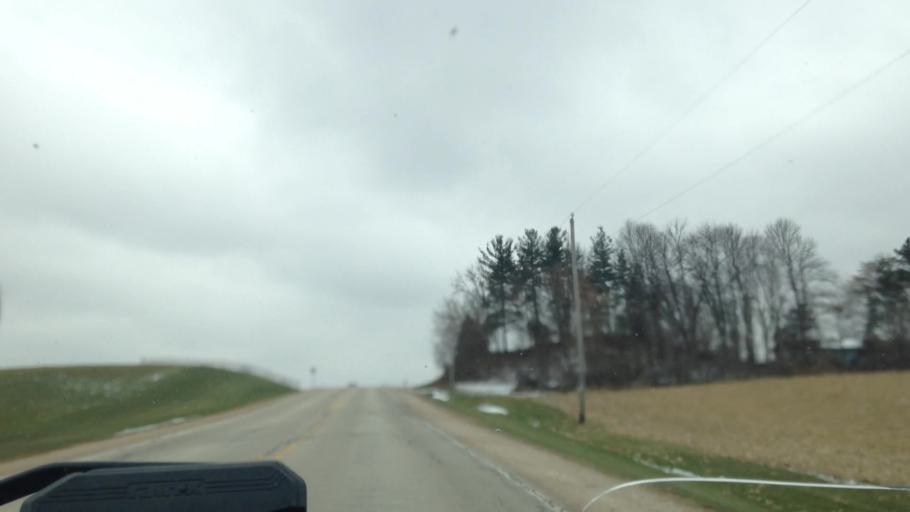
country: US
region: Wisconsin
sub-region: Dodge County
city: Mayville
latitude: 43.4534
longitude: -88.5000
